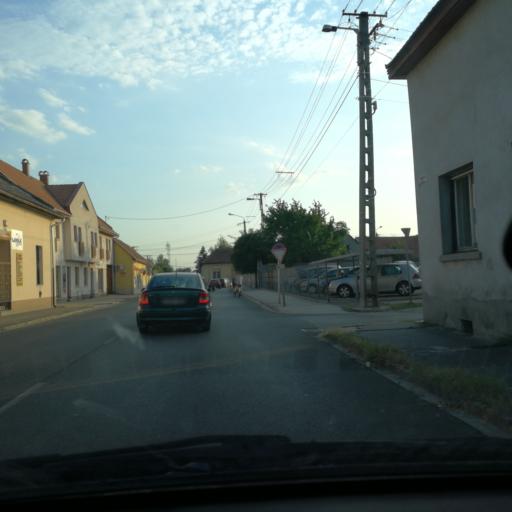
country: HU
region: Bacs-Kiskun
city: Kiskunmajsa
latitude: 46.4908
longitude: 19.7338
